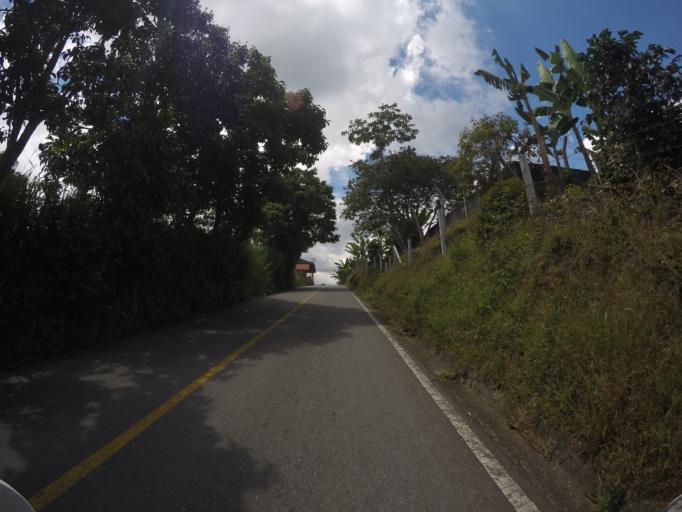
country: CO
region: Quindio
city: Quimbaya
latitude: 4.6318
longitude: -75.7111
